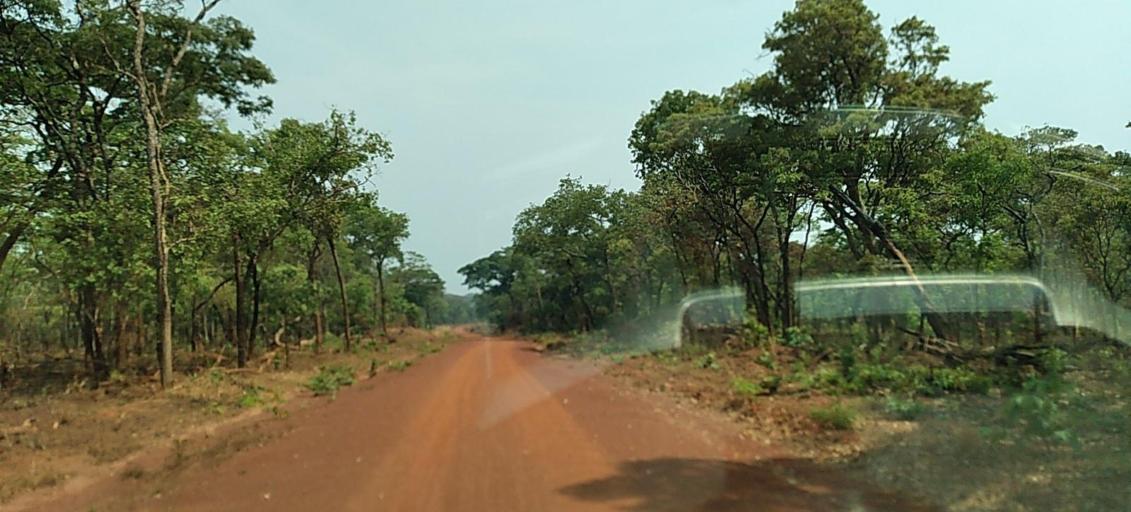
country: ZM
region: North-Western
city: Kansanshi
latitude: -12.0029
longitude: 26.8420
